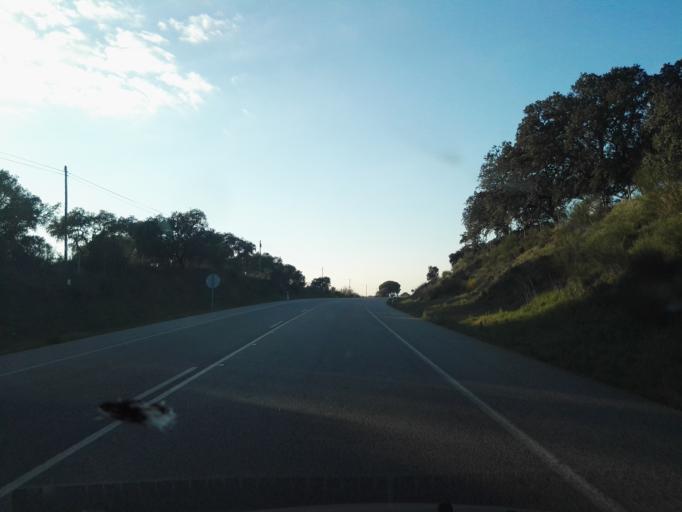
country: PT
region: Evora
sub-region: Montemor-O-Novo
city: Montemor-o-Novo
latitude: 38.6218
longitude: -8.0928
